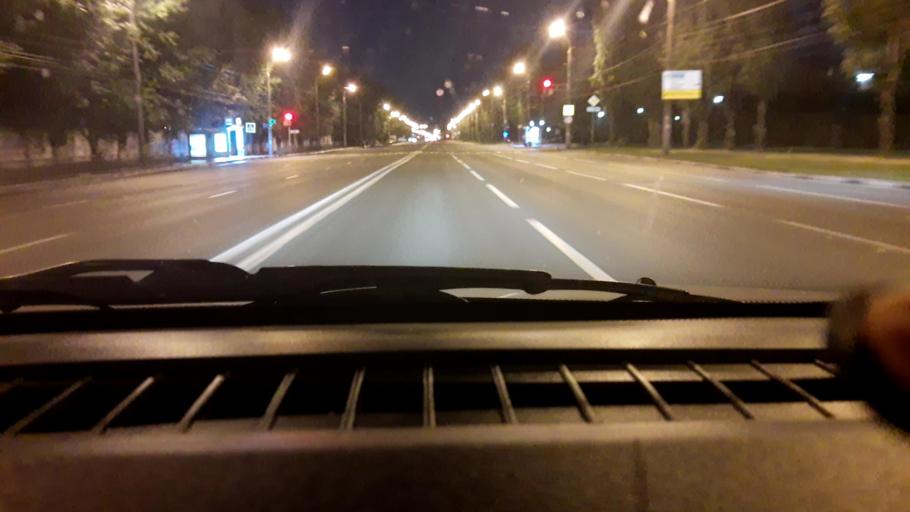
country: RU
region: Nizjnij Novgorod
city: Nizhniy Novgorod
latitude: 56.3203
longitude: 43.9391
